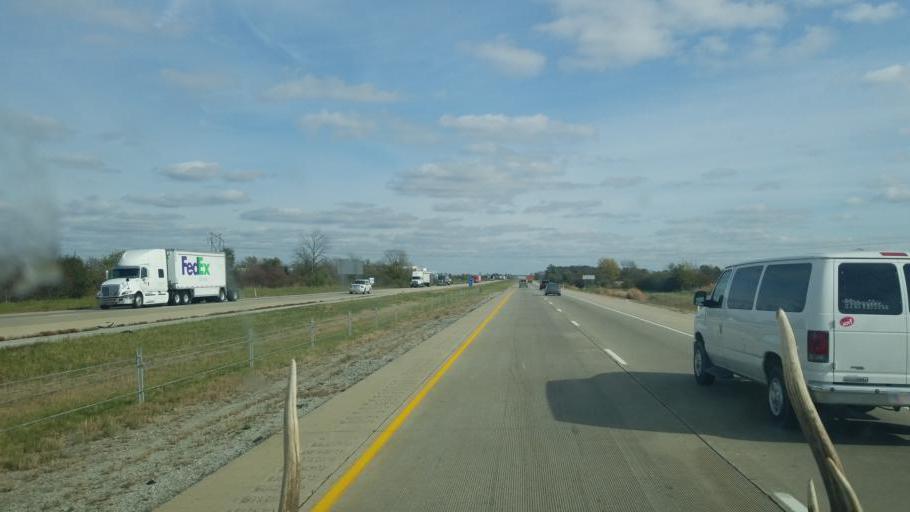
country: US
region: Indiana
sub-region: Marion County
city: Cumberland
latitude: 39.8195
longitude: -85.8932
